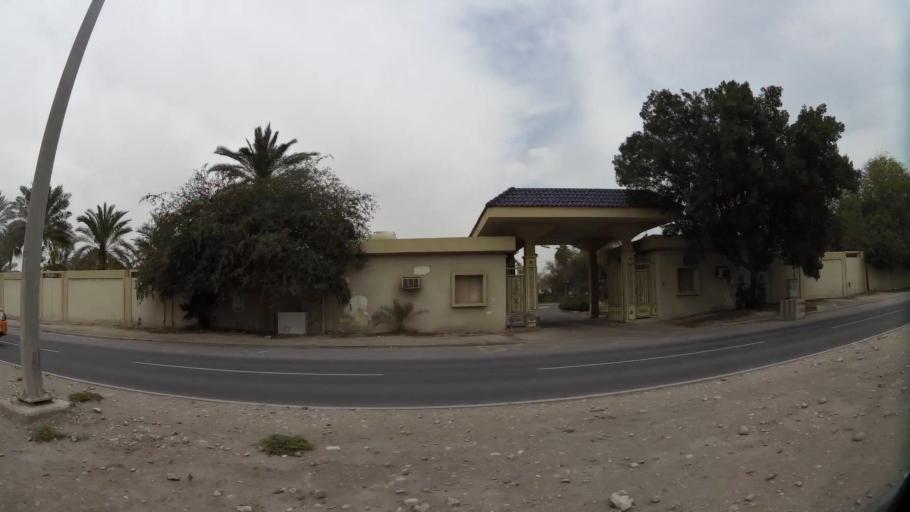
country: QA
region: Baladiyat ar Rayyan
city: Ar Rayyan
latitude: 25.2239
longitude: 51.4526
